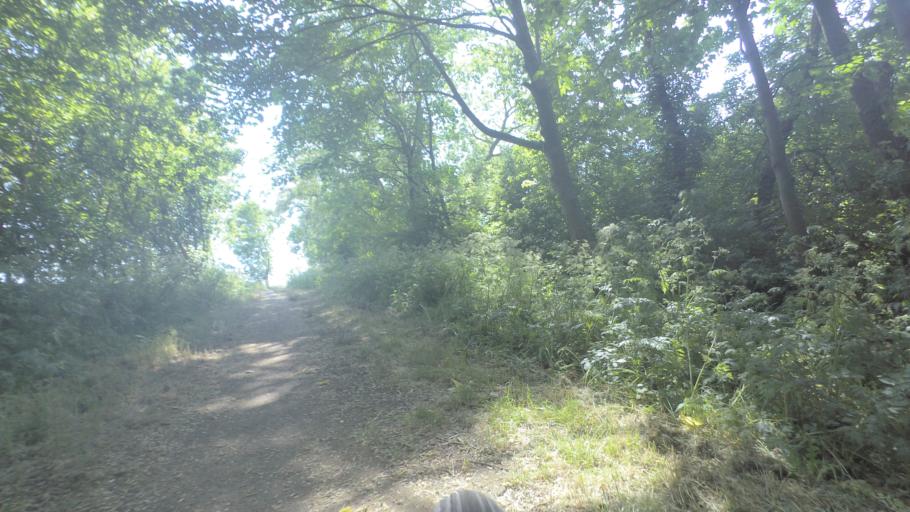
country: DE
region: Saxony-Anhalt
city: Frose
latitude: 51.8343
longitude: 11.3939
